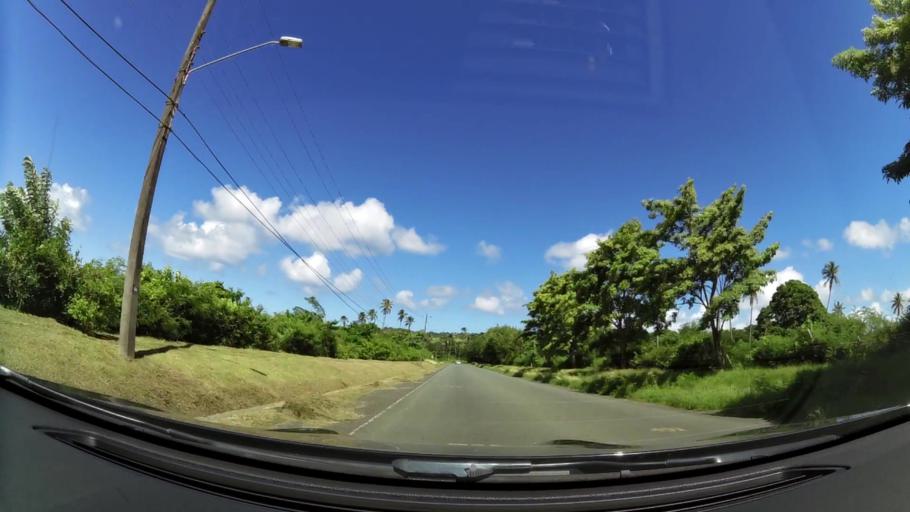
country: TT
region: Tobago
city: Scarborough
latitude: 11.1662
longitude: -60.7718
